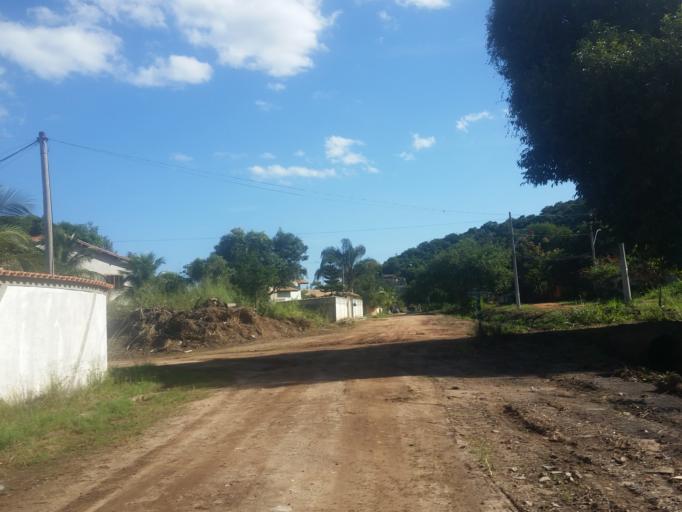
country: BR
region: Rio de Janeiro
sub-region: Marica
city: Marica
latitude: -22.9553
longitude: -42.9669
